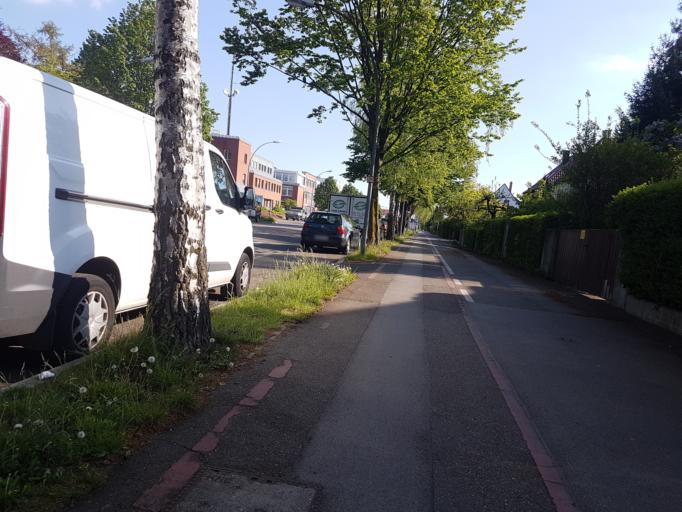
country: DE
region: Baden-Wuerttemberg
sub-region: Regierungsbezirk Stuttgart
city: Kornwestheim
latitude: 48.8583
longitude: 9.1852
